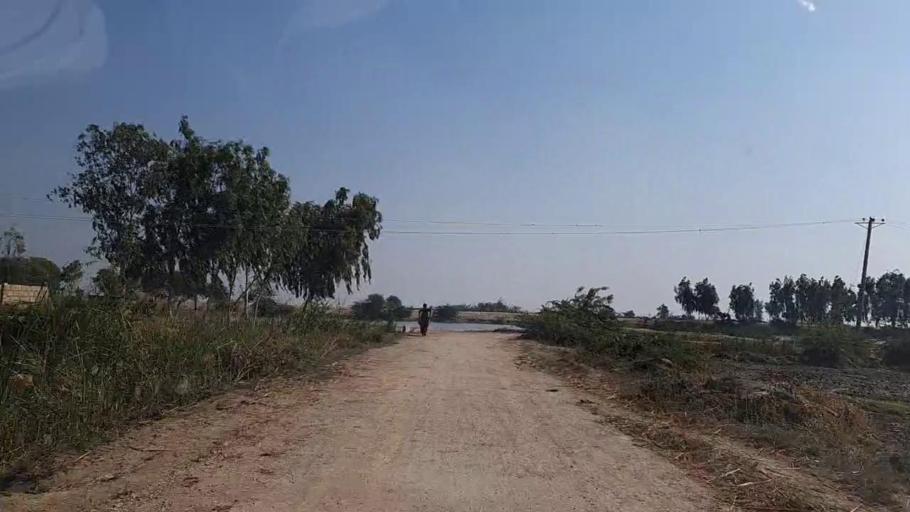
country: PK
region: Sindh
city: Thatta
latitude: 24.7963
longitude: 67.9772
